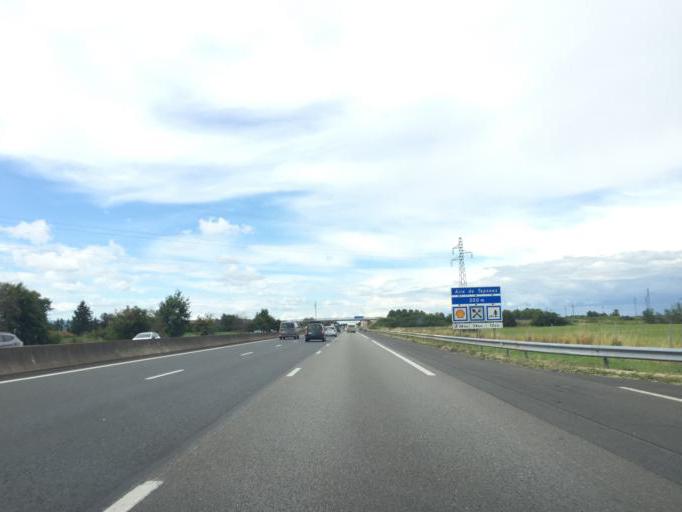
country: FR
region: Rhone-Alpes
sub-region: Departement de l'Ain
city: Guereins
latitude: 46.1284
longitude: 4.7652
